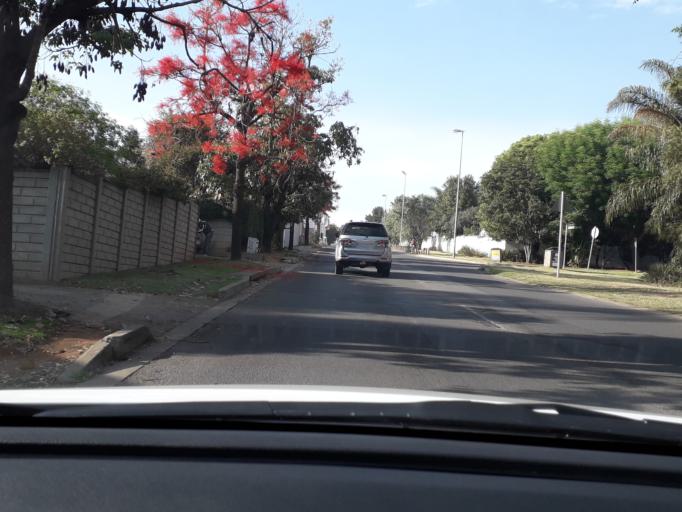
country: ZA
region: Gauteng
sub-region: City of Johannesburg Metropolitan Municipality
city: Roodepoort
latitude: -26.0766
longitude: 27.9455
